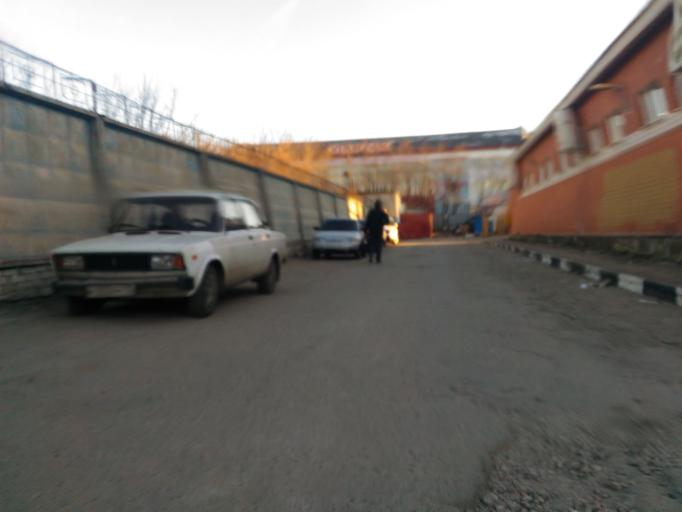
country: RU
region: Ulyanovsk
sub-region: Ulyanovskiy Rayon
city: Ulyanovsk
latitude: 54.3173
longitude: 48.3905
